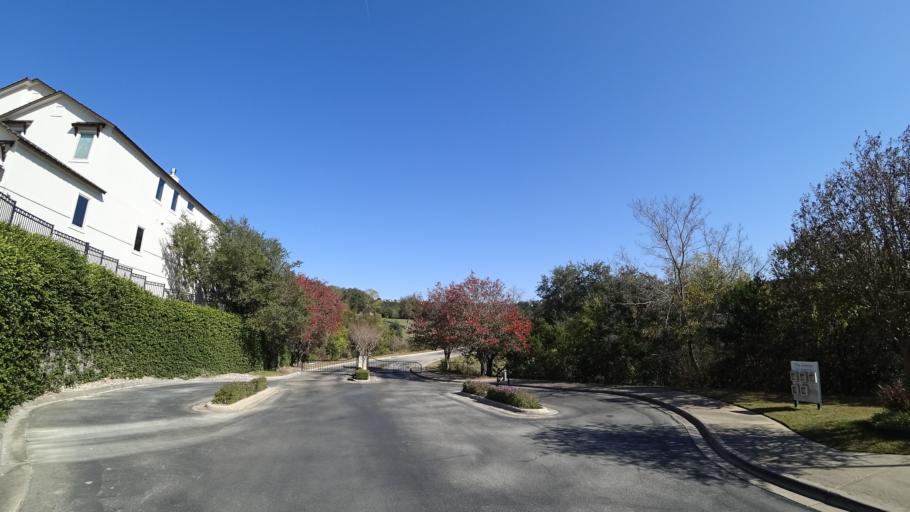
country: US
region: Texas
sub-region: Travis County
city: Lost Creek
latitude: 30.3659
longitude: -97.8596
